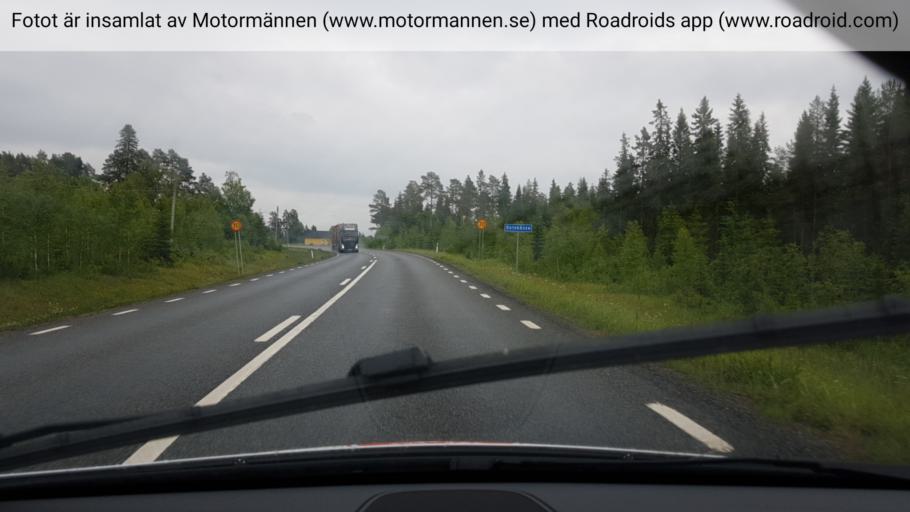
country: SE
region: Jaemtland
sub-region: OEstersunds Kommun
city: Lit
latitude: 63.3898
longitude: 14.9364
